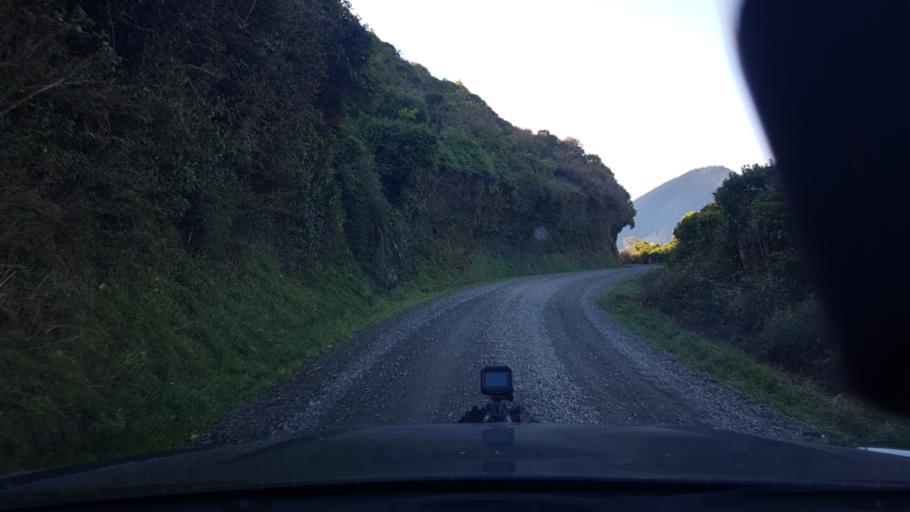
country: NZ
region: Marlborough
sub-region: Marlborough District
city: Picton
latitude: -41.2776
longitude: 173.7145
